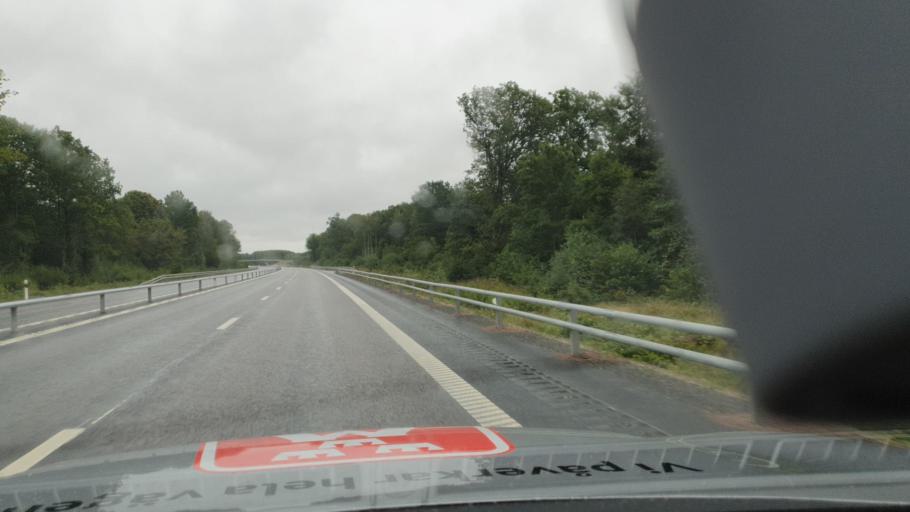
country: SE
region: Skane
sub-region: Kristianstads Kommun
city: Onnestad
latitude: 55.9614
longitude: 13.9937
